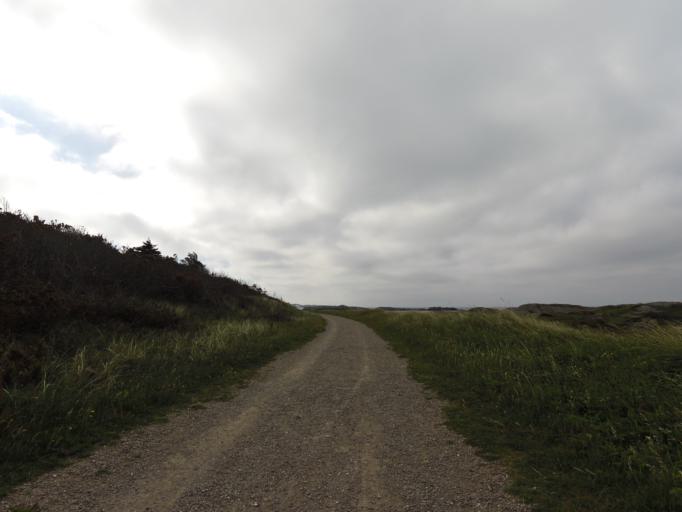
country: NO
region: Rogaland
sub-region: Ha
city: Vigrestad
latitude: 58.5270
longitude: 5.7755
